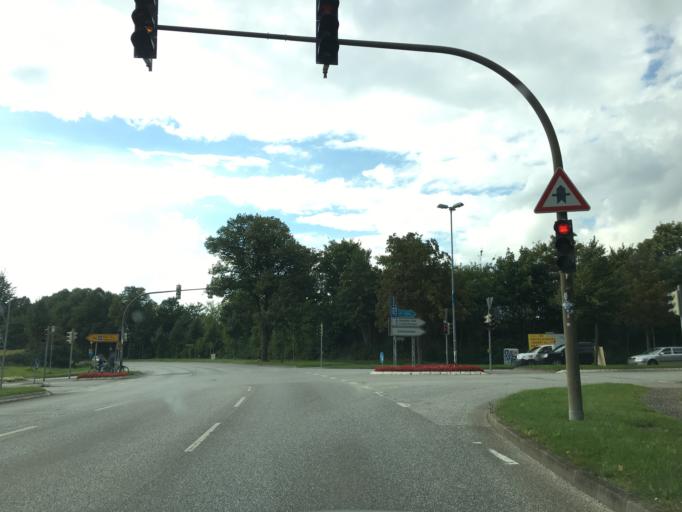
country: DE
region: Schleswig-Holstein
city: Heikendorf
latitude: 54.3740
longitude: 10.2224
